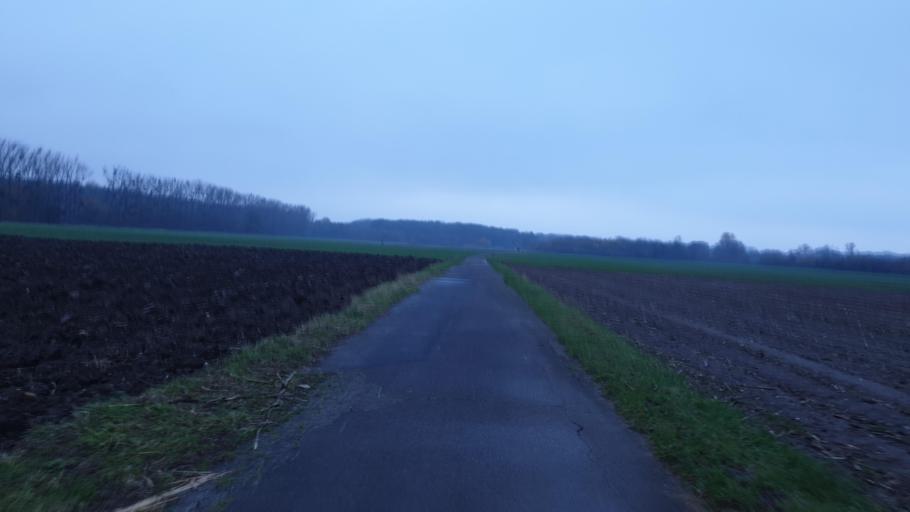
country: DE
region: North Rhine-Westphalia
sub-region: Regierungsbezirk Koln
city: Kerpen
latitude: 50.9211
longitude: 6.6911
